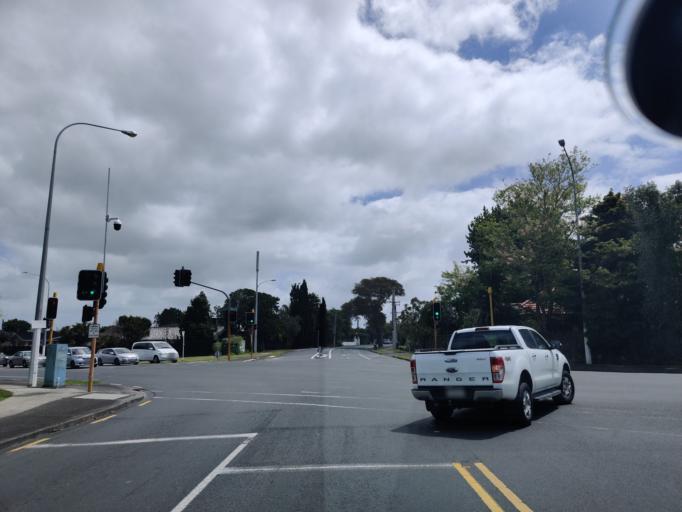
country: NZ
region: Auckland
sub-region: Auckland
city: Mangere
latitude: -36.9549
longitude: 174.7910
